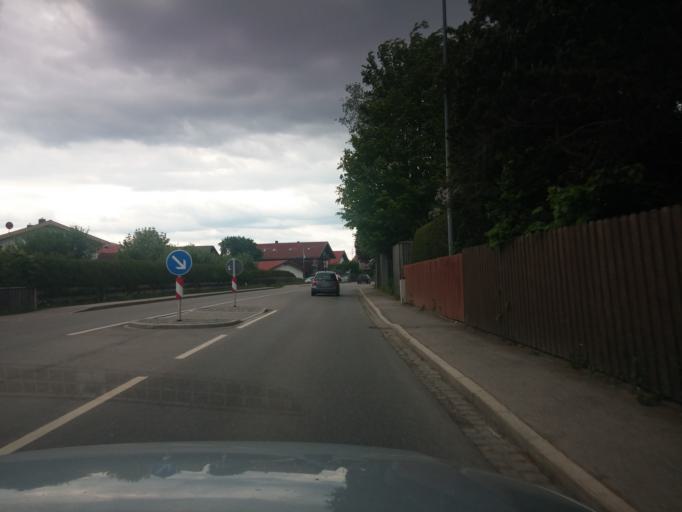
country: DE
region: Bavaria
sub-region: Upper Bavaria
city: Holzkirchen
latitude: 47.8710
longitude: 11.6945
